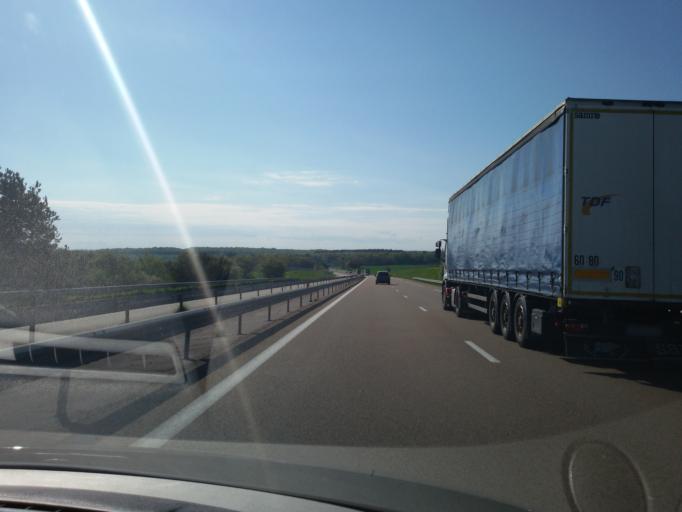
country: FR
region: Bourgogne
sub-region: Departement de l'Yonne
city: Vermenton
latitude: 47.7240
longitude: 3.7524
